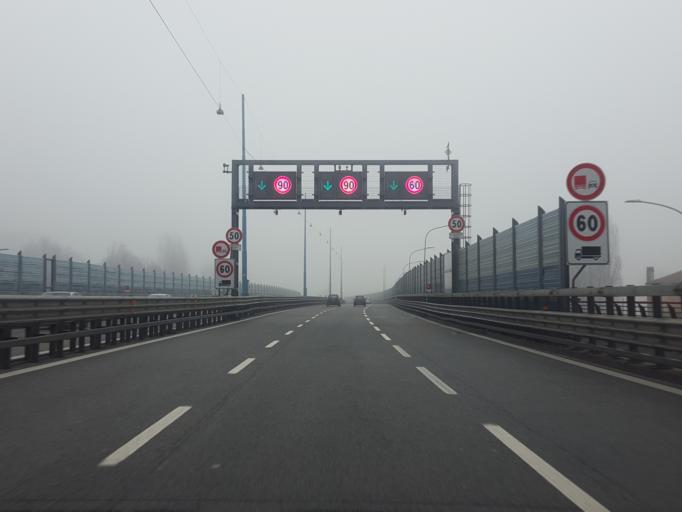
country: IT
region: Veneto
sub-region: Provincia di Venezia
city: Mestre
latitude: 45.4734
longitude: 12.2070
